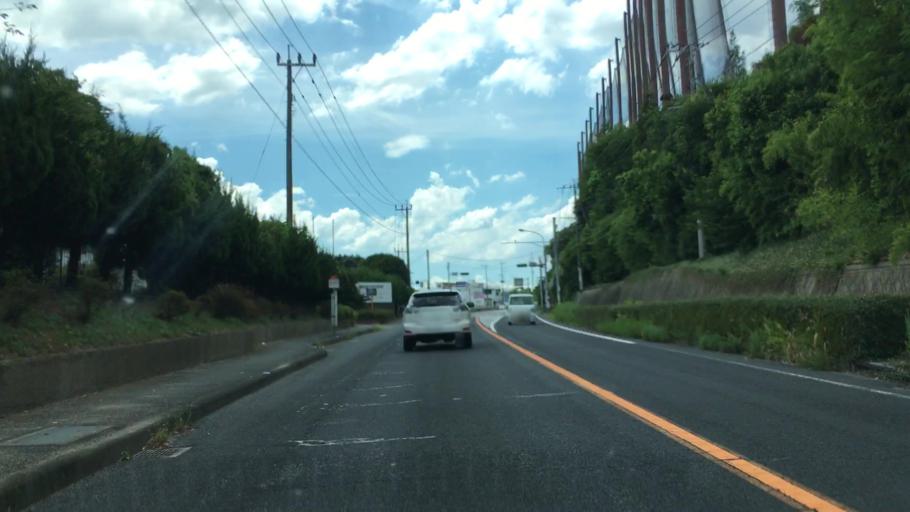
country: JP
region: Saga Prefecture
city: Tosu
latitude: 33.3600
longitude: 130.4945
